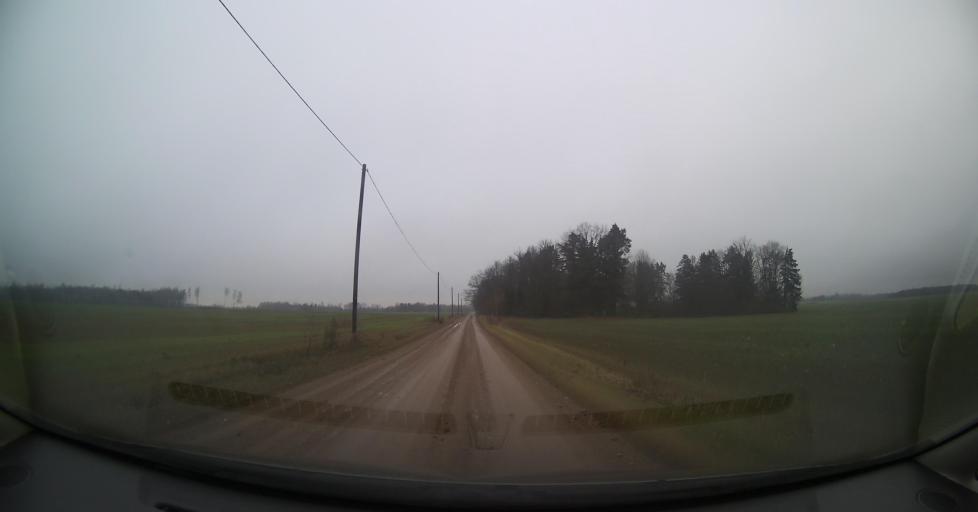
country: EE
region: Tartu
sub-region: Tartu linn
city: Tartu
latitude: 58.3819
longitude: 26.9266
